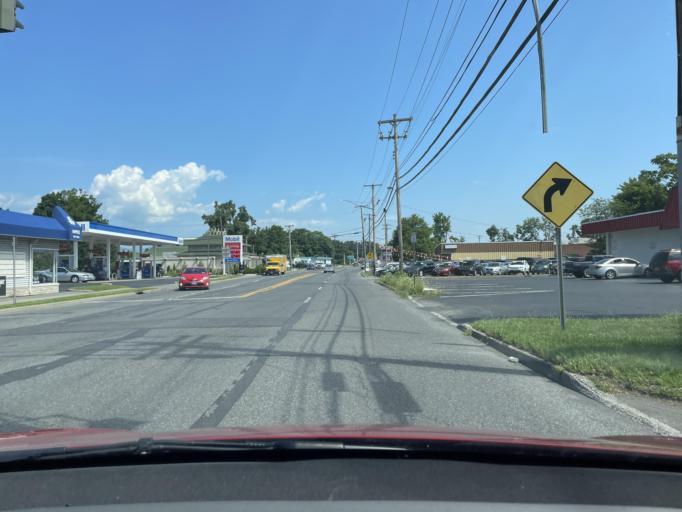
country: US
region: New York
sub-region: Ulster County
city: Lincoln Park
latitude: 41.9548
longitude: -73.9944
